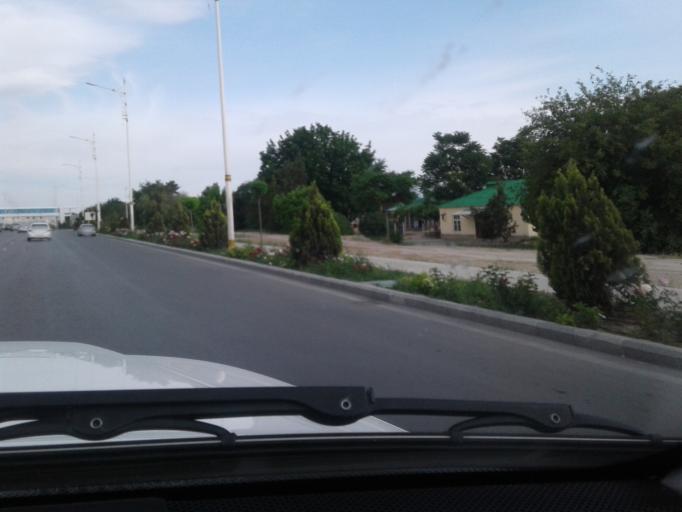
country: TM
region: Ahal
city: Ashgabat
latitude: 37.9720
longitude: 58.3499
